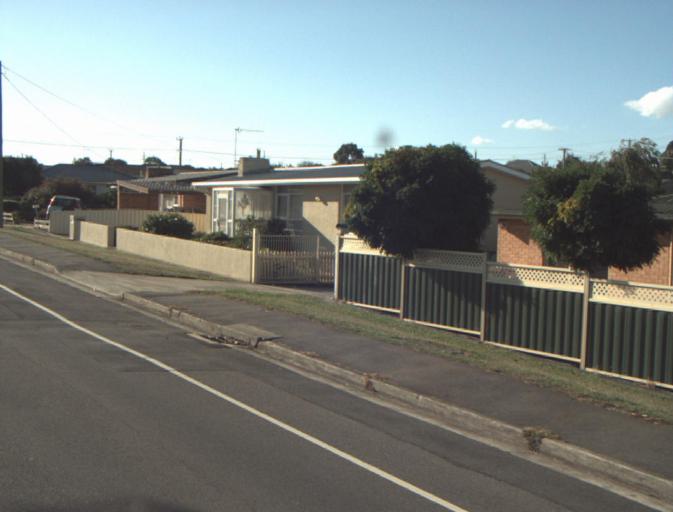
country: AU
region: Tasmania
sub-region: Launceston
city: Summerhill
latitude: -41.4690
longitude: 147.1321
